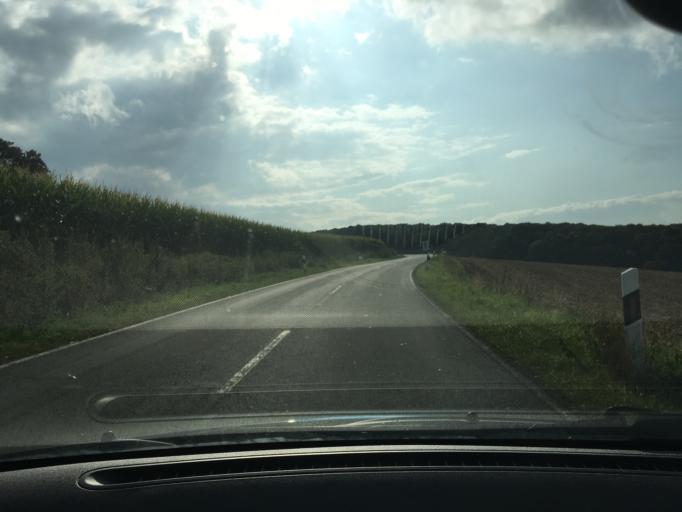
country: DE
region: Lower Saxony
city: Barsinghausen
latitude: 52.2519
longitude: 9.4453
